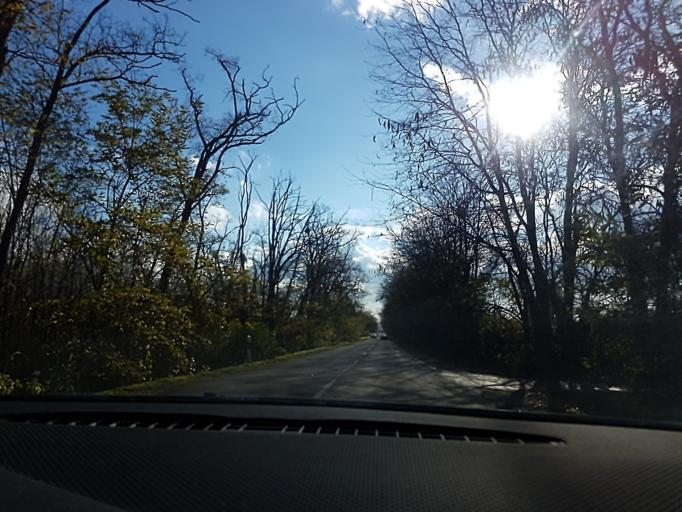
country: HU
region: Pest
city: Szada
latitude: 47.6214
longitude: 19.3260
